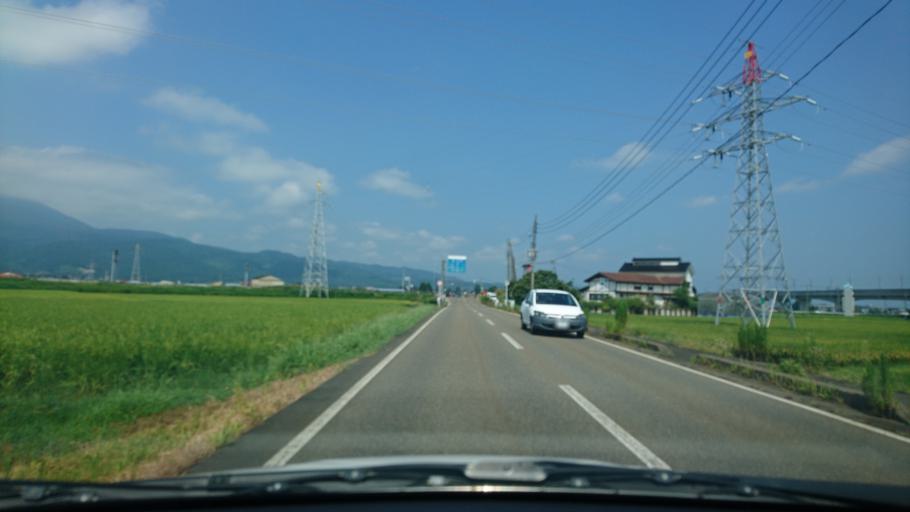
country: JP
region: Niigata
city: Arai
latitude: 37.0643
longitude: 138.2649
